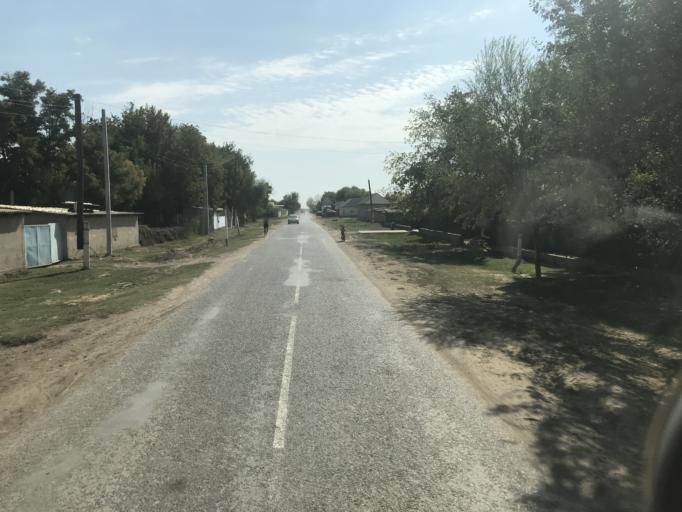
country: KZ
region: Ongtustik Qazaqstan
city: Myrzakent
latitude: 40.6642
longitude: 68.6240
